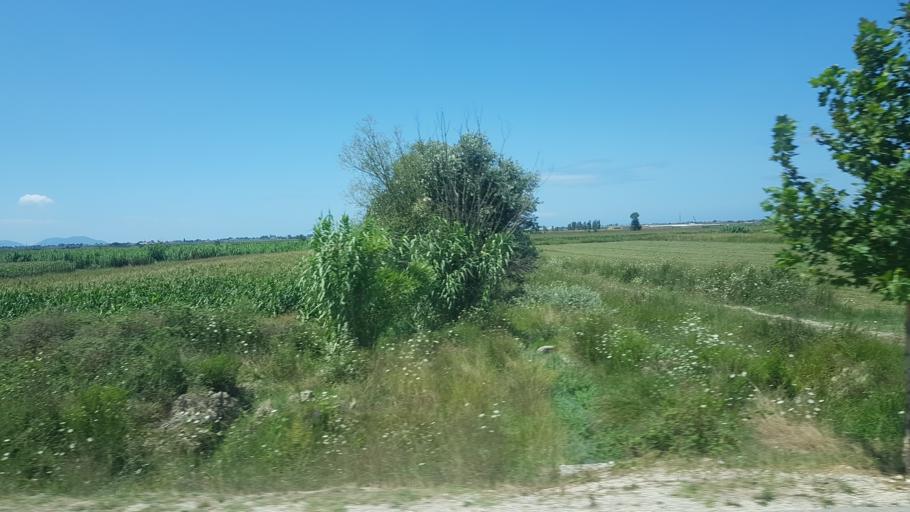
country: AL
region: Fier
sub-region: Rrethi i Fierit
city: Frakulla e Madhe
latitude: 40.6592
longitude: 19.4899
